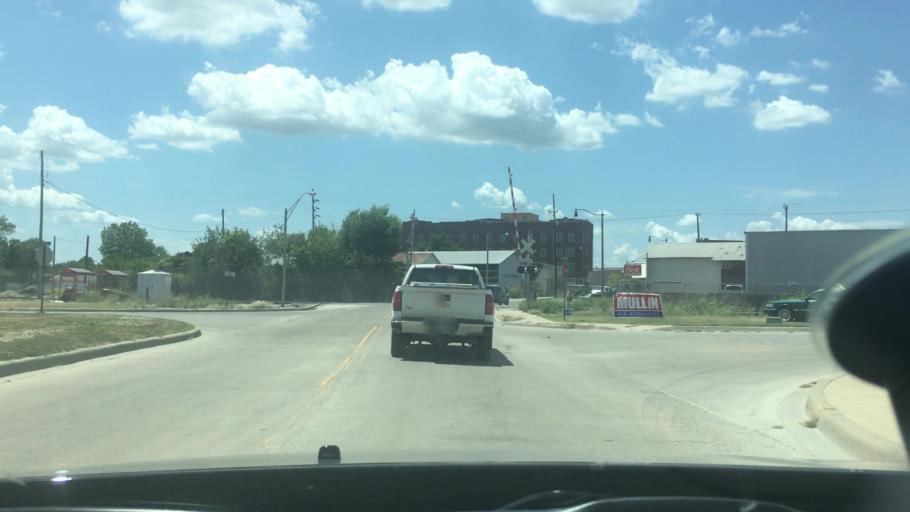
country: US
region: Oklahoma
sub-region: Bryan County
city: Durant
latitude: 33.9903
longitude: -96.3737
